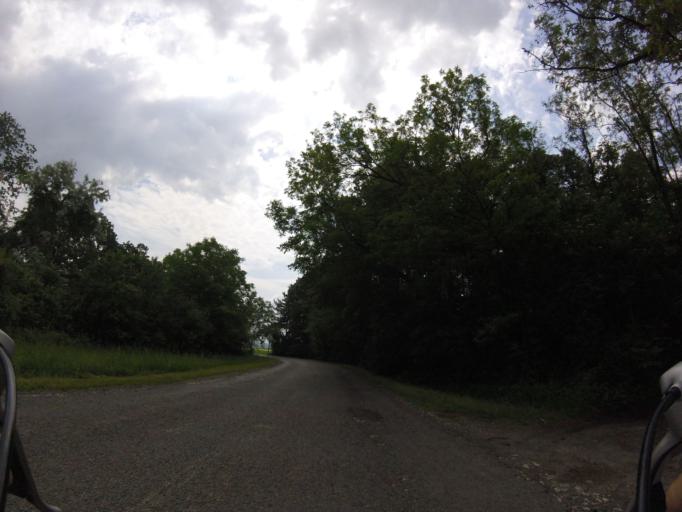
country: HU
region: Baranya
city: Kozarmisleny
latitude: 46.0768
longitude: 18.3514
